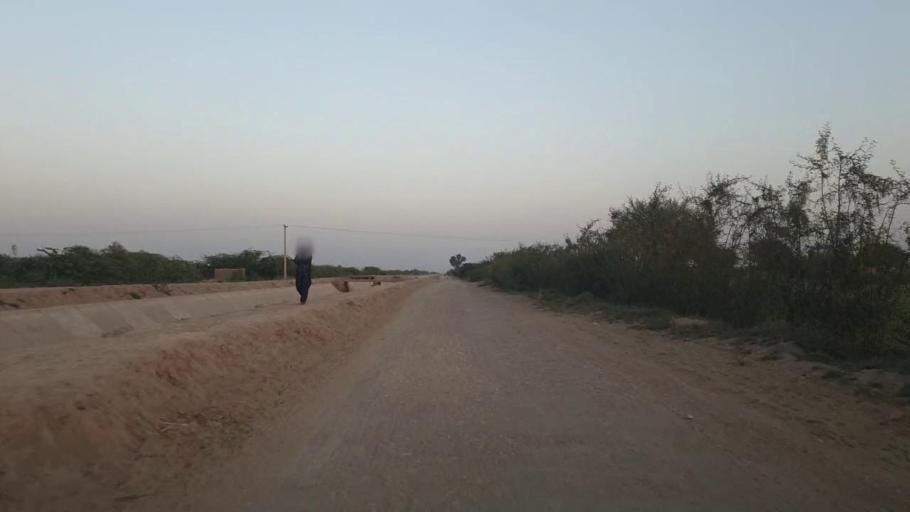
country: PK
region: Sindh
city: Umarkot
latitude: 25.4298
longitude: 69.6530
